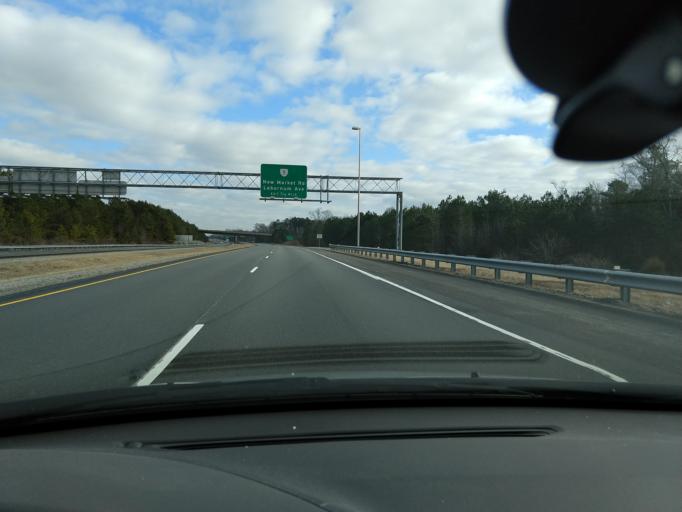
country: US
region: Virginia
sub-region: Chesterfield County
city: Bensley
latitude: 37.4489
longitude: -77.3998
